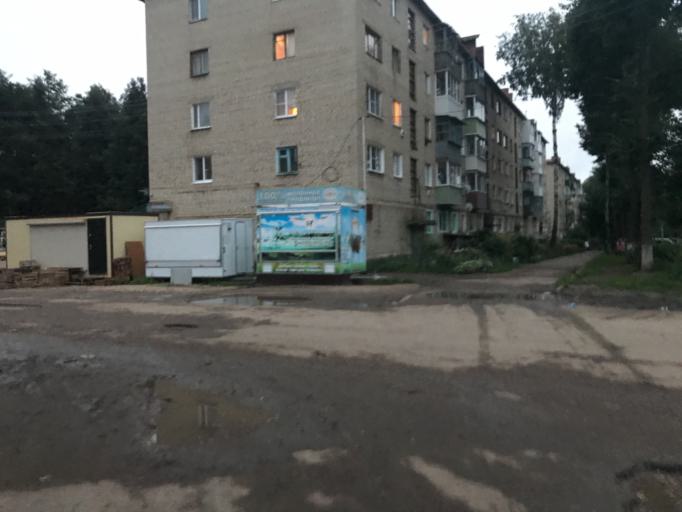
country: RU
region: Tula
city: Priupskiy
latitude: 53.9372
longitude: 37.6991
